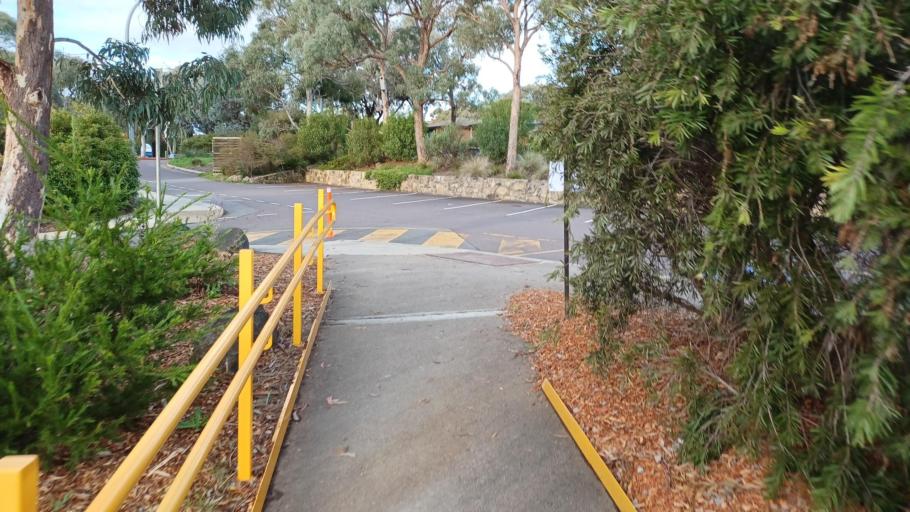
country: AU
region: Australian Capital Territory
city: Belconnen
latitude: -35.1920
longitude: 149.0433
